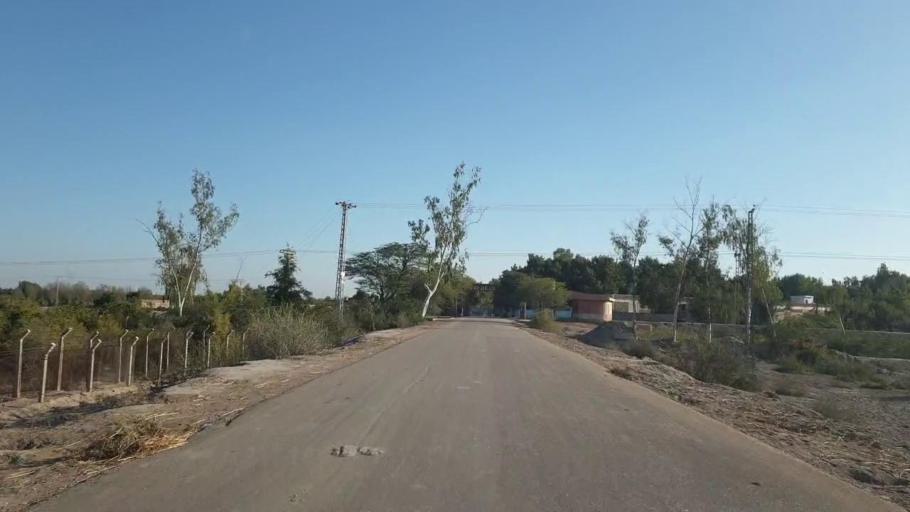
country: PK
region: Sindh
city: Dokri
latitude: 27.3308
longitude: 68.1312
